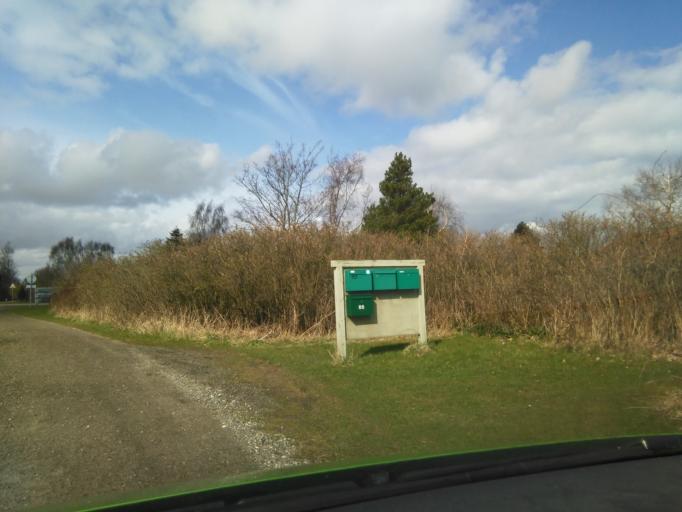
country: DK
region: Central Jutland
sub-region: Arhus Kommune
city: Beder
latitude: 56.0185
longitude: 10.2729
